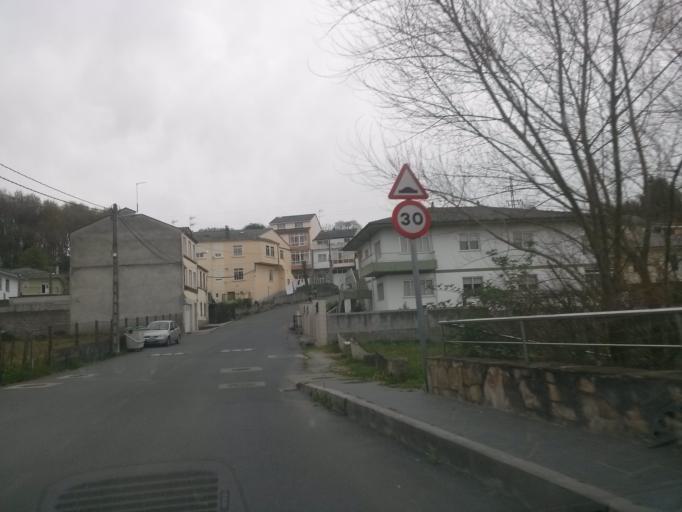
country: ES
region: Galicia
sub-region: Provincia de Lugo
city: Lugo
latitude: 43.0171
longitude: -7.5464
